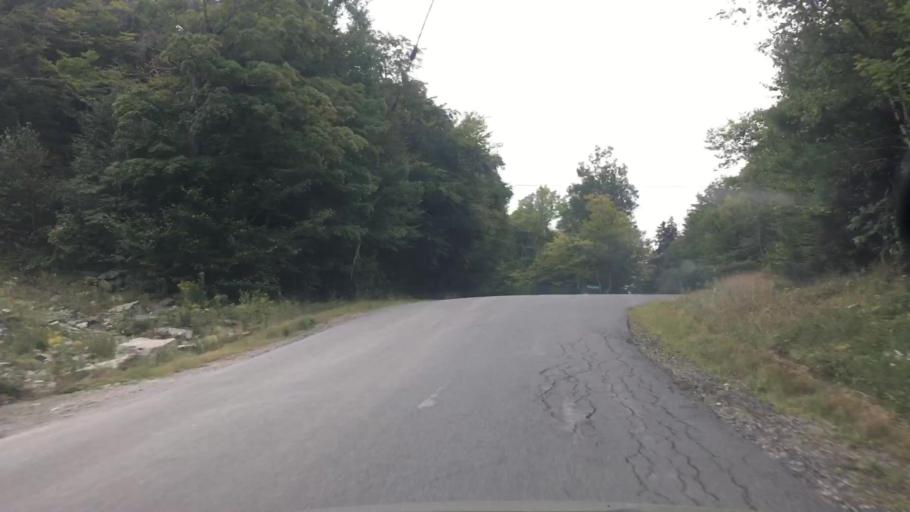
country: US
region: Vermont
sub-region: Windham County
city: Dover
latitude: 42.8398
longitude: -72.8224
